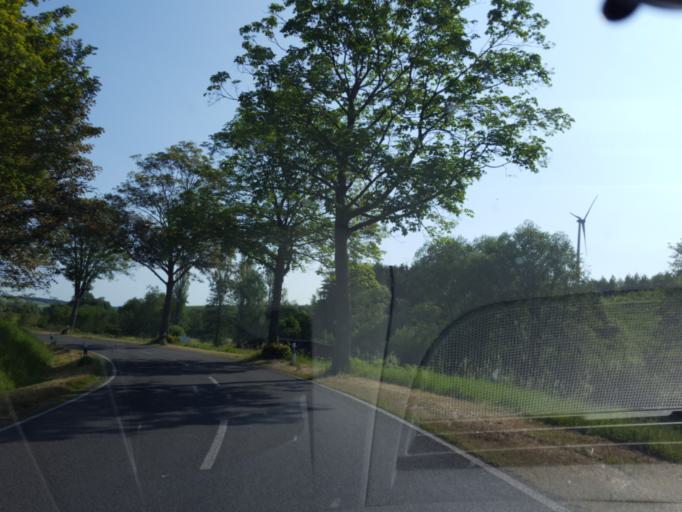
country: DE
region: Lower Saxony
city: Wulften
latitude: 51.6646
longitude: 10.1926
